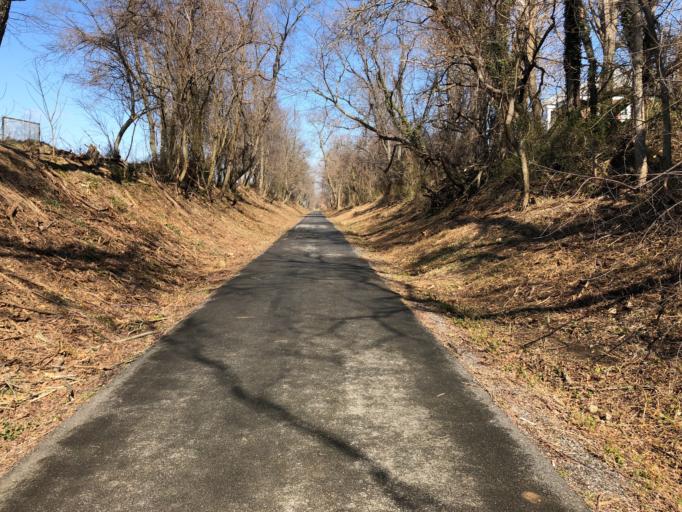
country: US
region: Maryland
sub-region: Kent County
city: Chestertown
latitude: 39.2195
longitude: -76.0721
